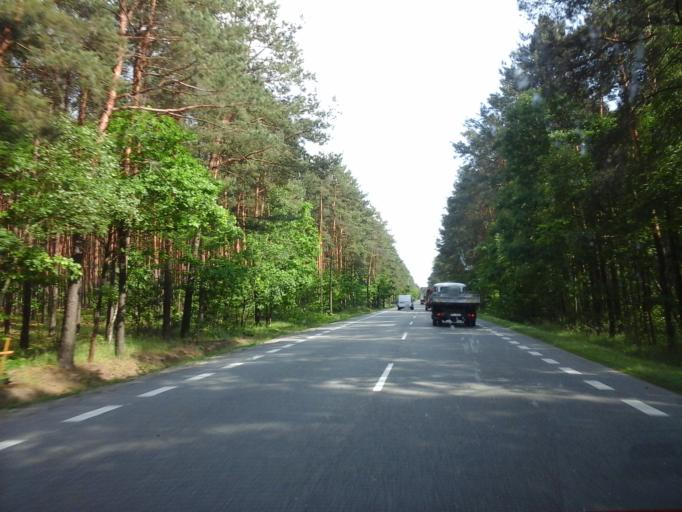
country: PL
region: Swietokrzyskie
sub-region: Powiat konecki
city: Ruda Maleniecka
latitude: 51.1591
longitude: 20.2303
